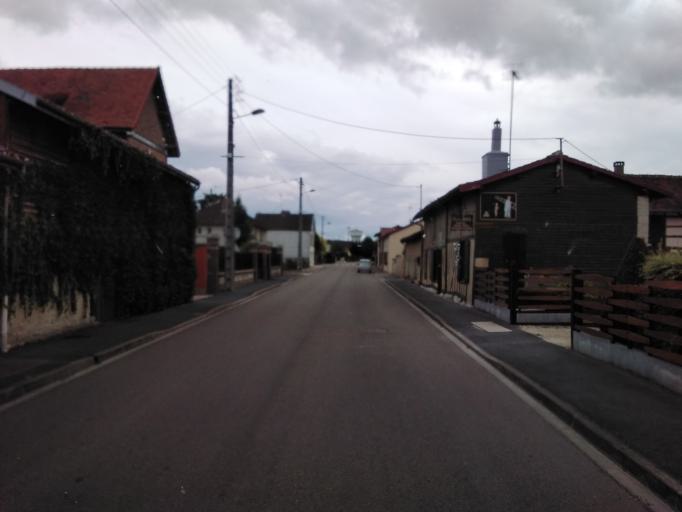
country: FR
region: Champagne-Ardenne
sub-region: Departement de l'Aube
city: Brienne-le-Chateau
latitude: 48.3883
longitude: 4.5288
